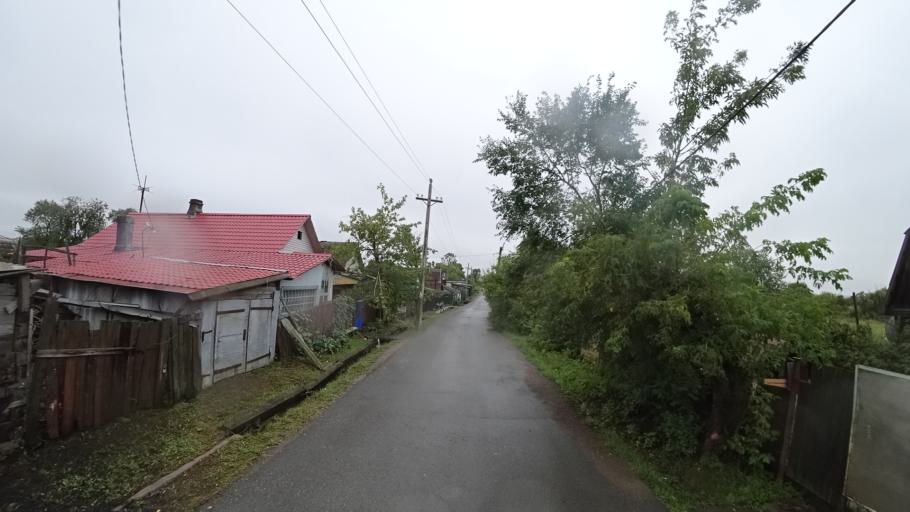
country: RU
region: Primorskiy
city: Monastyrishche
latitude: 44.1927
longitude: 132.4210
